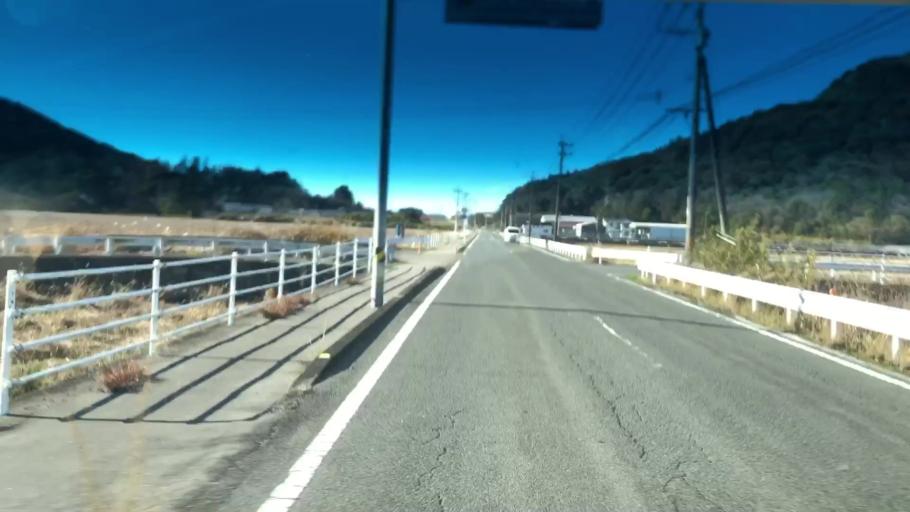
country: JP
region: Kagoshima
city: Satsumasendai
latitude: 31.8178
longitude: 130.2688
